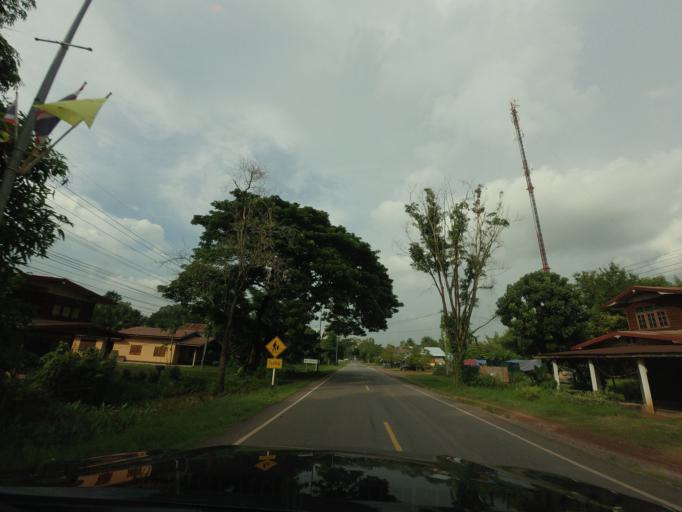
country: TH
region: Changwat Nong Bua Lamphu
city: Suwannakhuha
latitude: 17.5538
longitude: 102.3910
